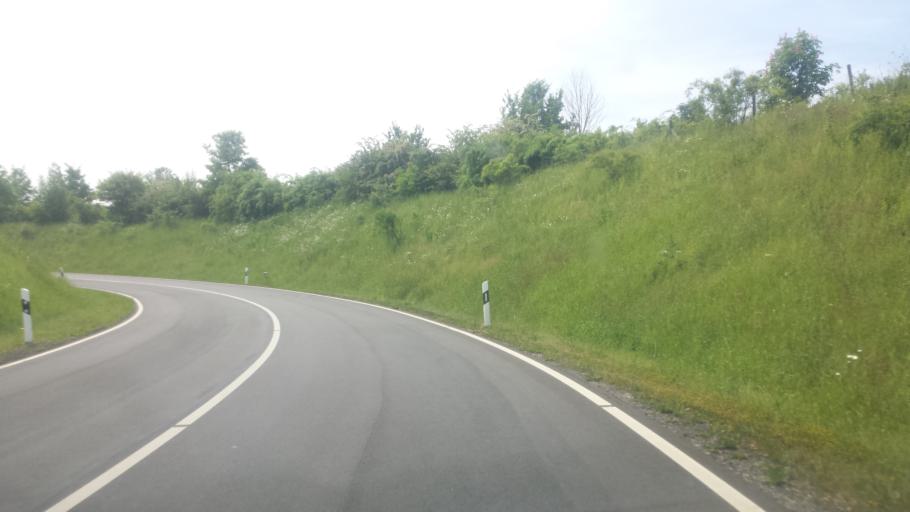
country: DE
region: Hesse
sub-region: Regierungsbezirk Darmstadt
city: Bad Vilbel
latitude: 50.2109
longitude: 8.7346
